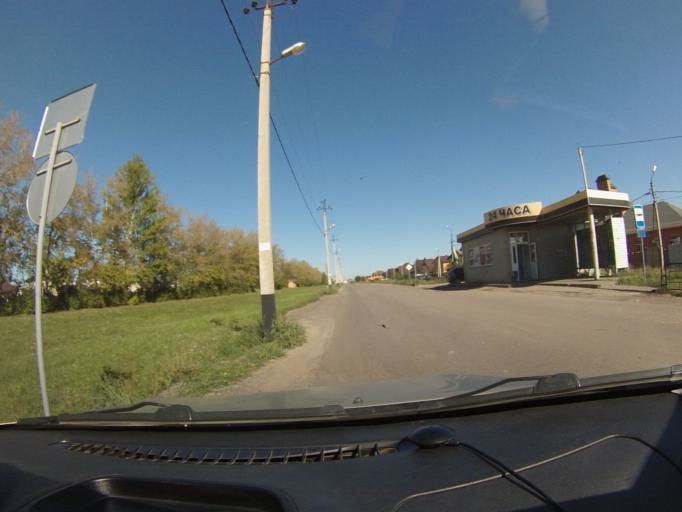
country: RU
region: Tambov
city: Tambov
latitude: 52.7709
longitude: 41.3702
